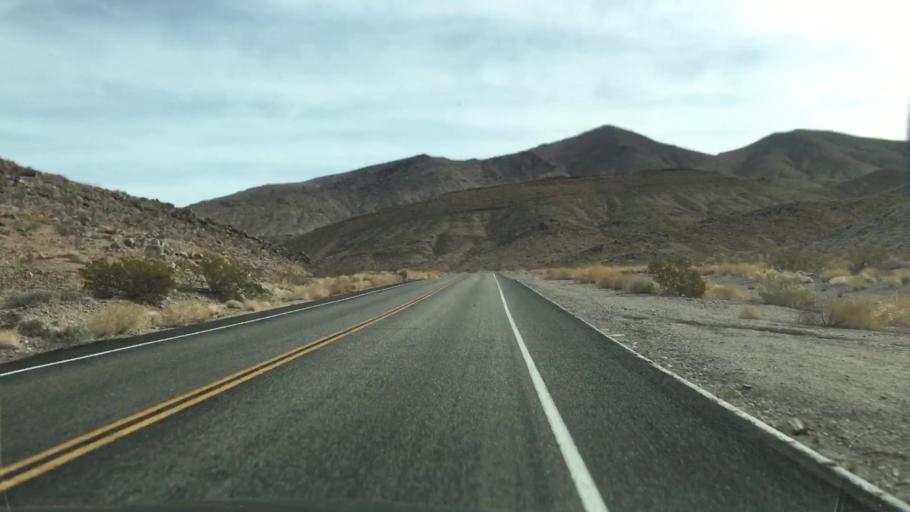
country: US
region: Nevada
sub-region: Nye County
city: Beatty
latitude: 36.7457
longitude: -116.9461
